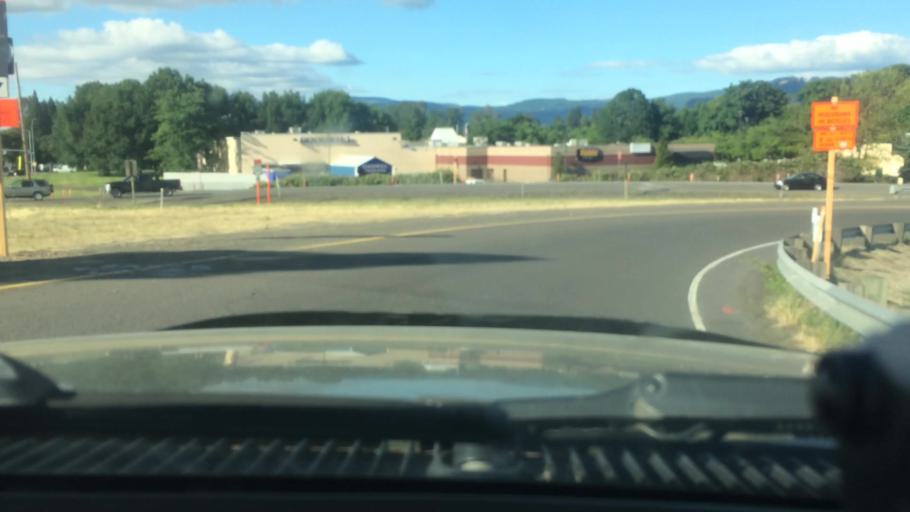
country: US
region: Oregon
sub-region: Lane County
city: Eugene
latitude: 44.0922
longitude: -123.0987
